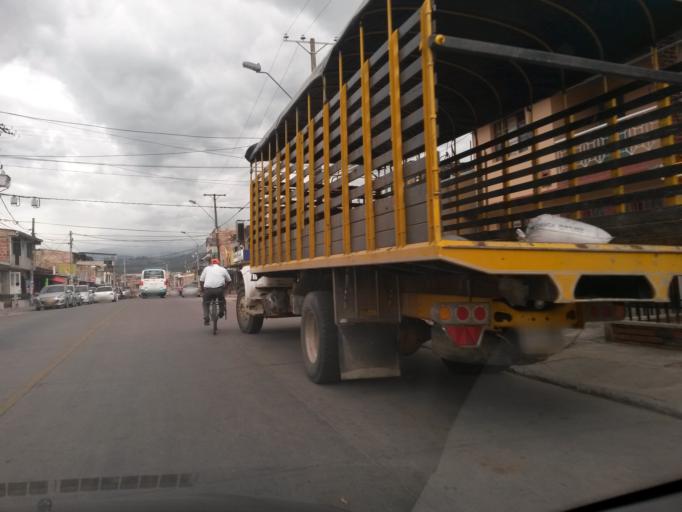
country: CO
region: Cauca
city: Popayan
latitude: 2.4445
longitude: -76.6201
